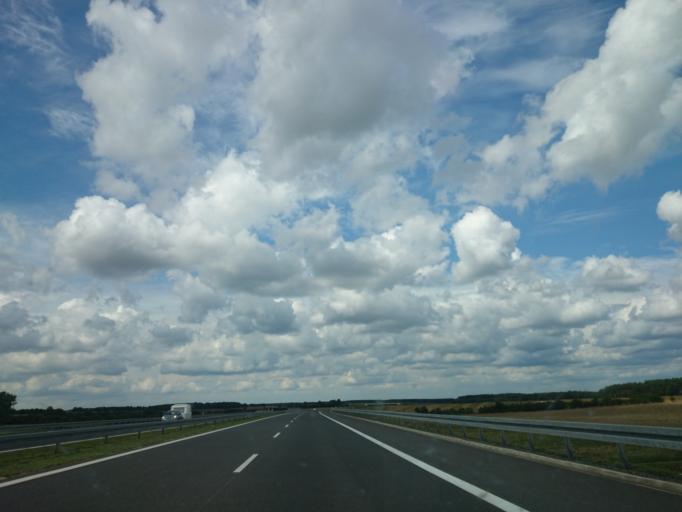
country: PL
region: Lubusz
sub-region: Powiat miedzyrzecki
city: Miedzyrzecz
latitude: 52.3651
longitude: 15.5488
